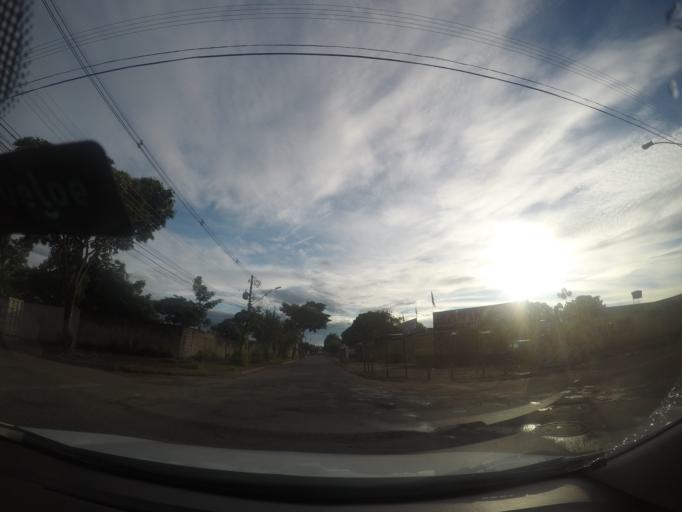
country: BR
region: Goias
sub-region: Goiania
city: Goiania
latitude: -16.6488
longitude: -49.3336
